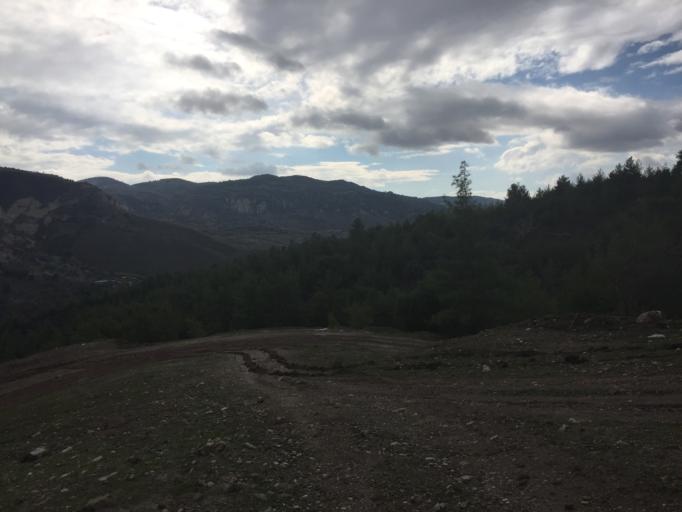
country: CY
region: Limassol
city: Pachna
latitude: 34.8852
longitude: 32.6702
